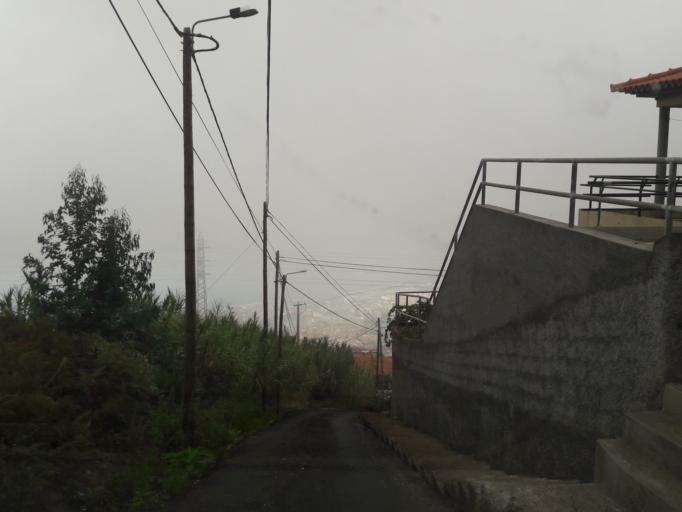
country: PT
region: Madeira
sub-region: Funchal
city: Nossa Senhora do Monte
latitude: 32.6676
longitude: -16.8893
